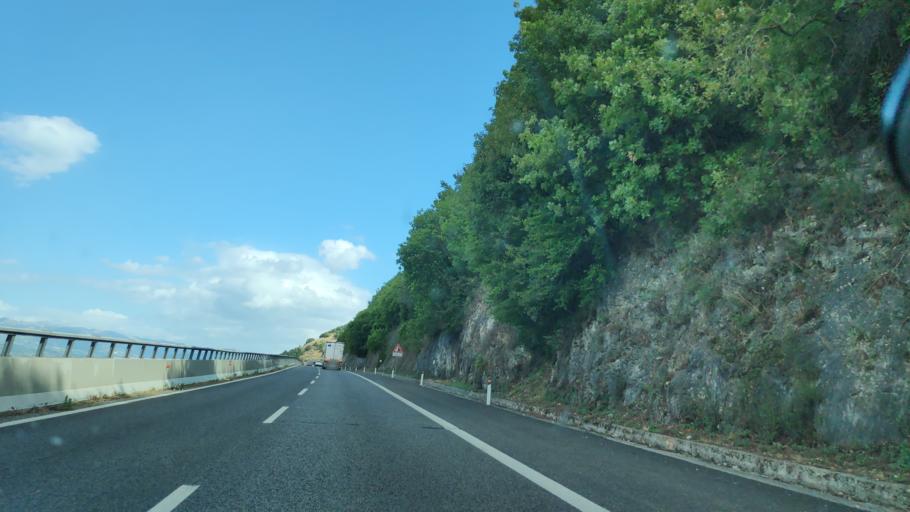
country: IT
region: Campania
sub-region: Provincia di Salerno
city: Sicignano degli Alburni
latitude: 40.5881
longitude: 15.3346
